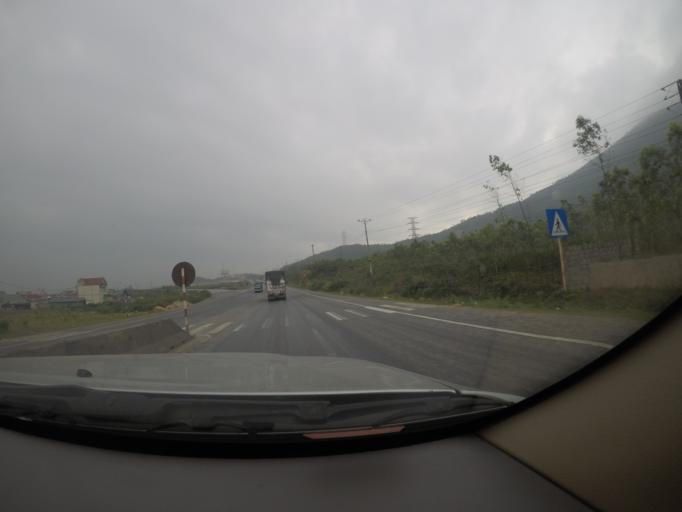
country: VN
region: Ha Tinh
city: Ky Anh
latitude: 17.9961
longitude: 106.4590
